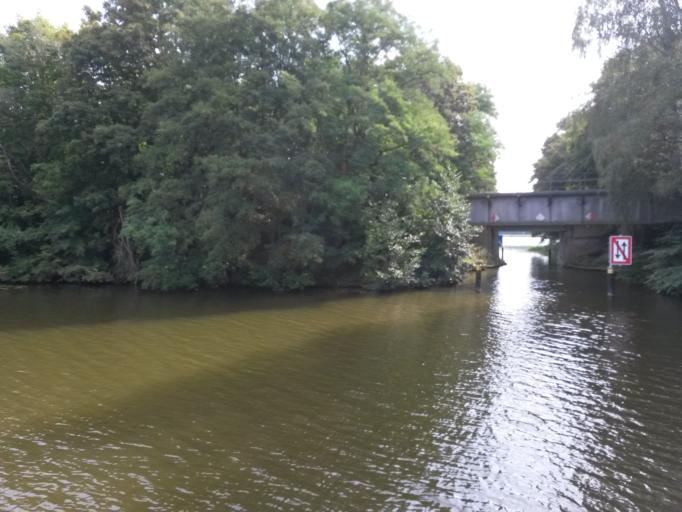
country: DE
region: Brandenburg
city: Templin
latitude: 53.1319
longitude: 13.5498
